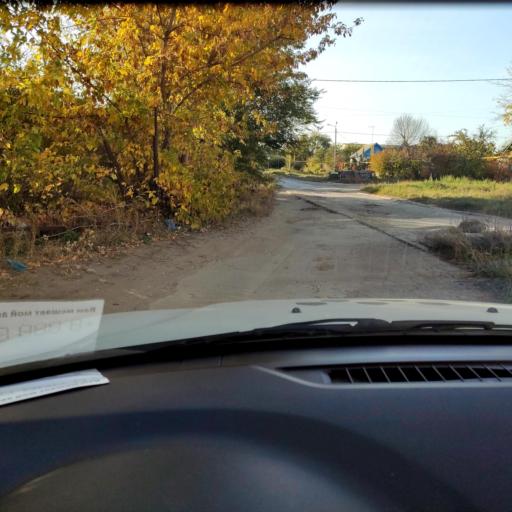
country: RU
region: Samara
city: Tol'yatti
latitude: 53.5384
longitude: 49.4032
